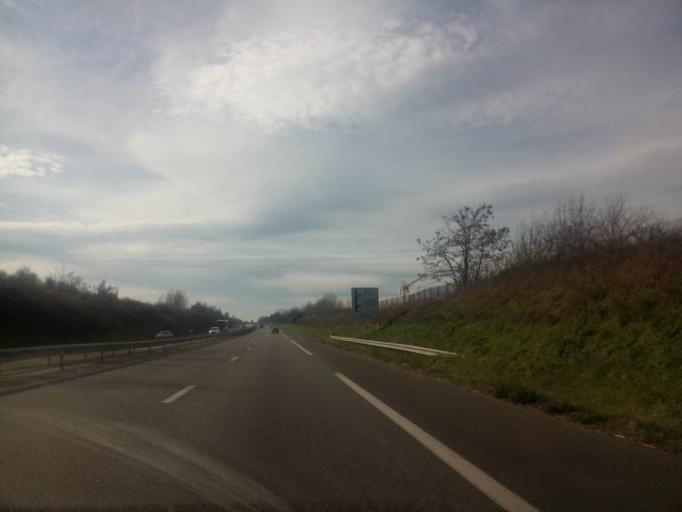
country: FR
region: Rhone-Alpes
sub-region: Departement du Rhone
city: Pierre-Benite
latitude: 45.6902
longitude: 4.8163
